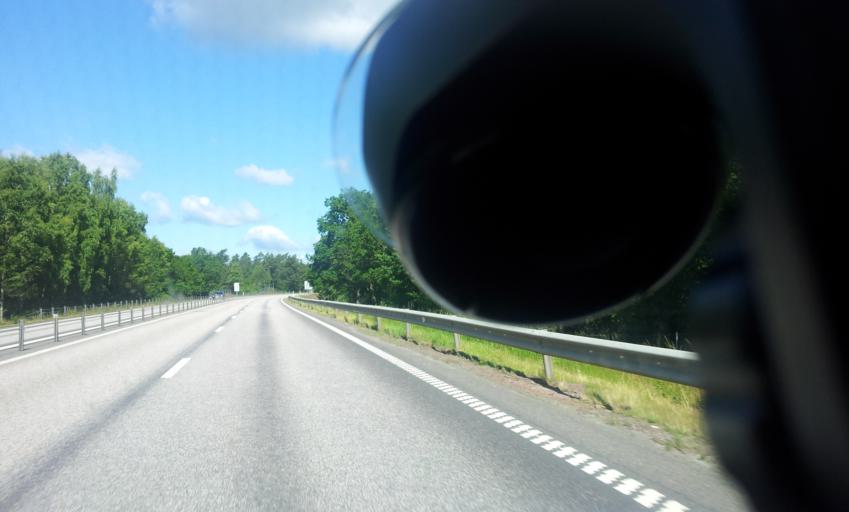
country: SE
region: Kalmar
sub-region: Oskarshamns Kommun
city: Paskallavik
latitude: 57.1573
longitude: 16.4530
